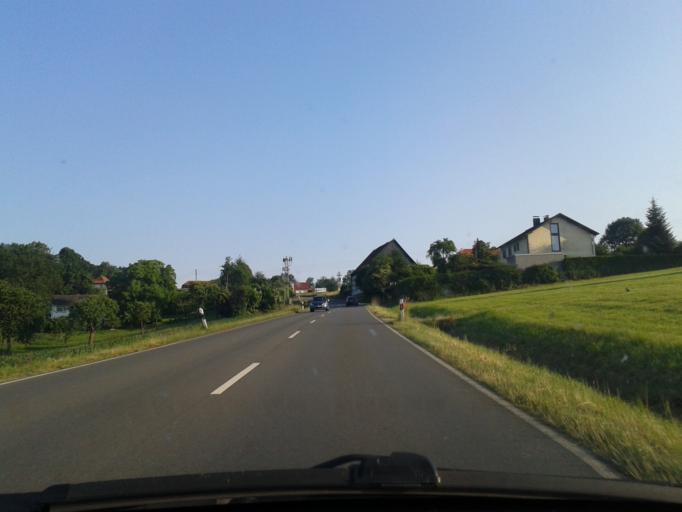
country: DE
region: North Rhine-Westphalia
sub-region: Regierungsbezirk Detmold
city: Detmold
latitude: 51.9647
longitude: 8.9105
